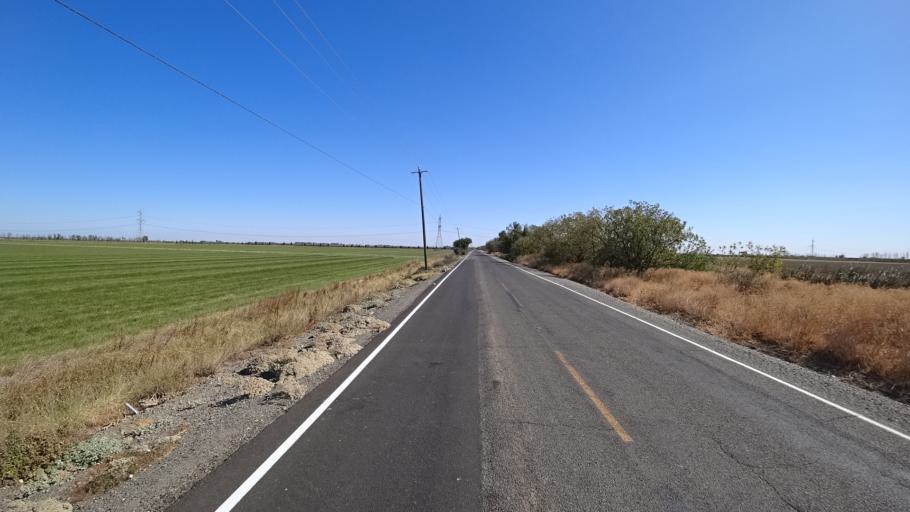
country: US
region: California
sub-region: Yolo County
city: Winters
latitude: 38.5620
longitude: -121.9141
